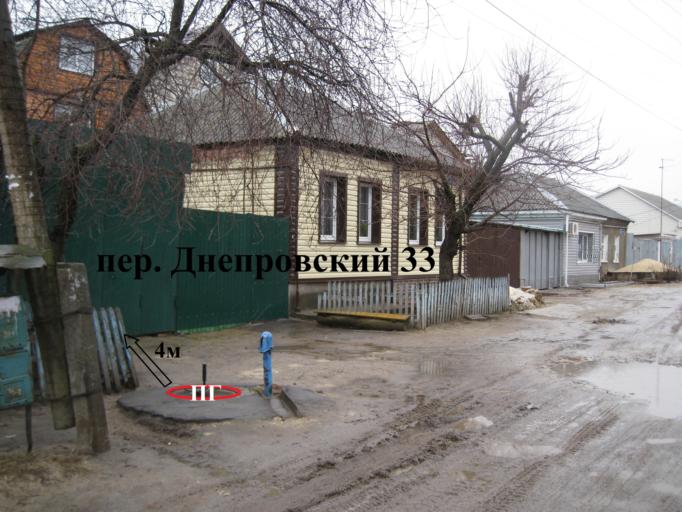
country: RU
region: Voronezj
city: Voronezh
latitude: 51.6261
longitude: 39.1927
